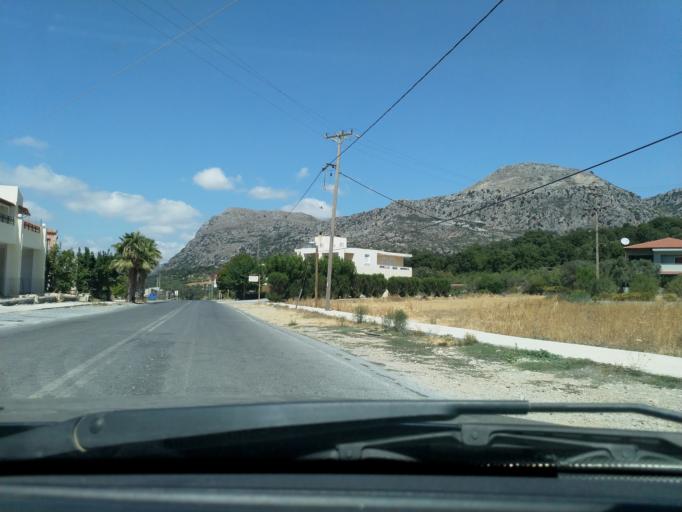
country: GR
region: Crete
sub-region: Nomos Rethymnis
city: Agia Foteini
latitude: 35.1885
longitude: 24.5537
